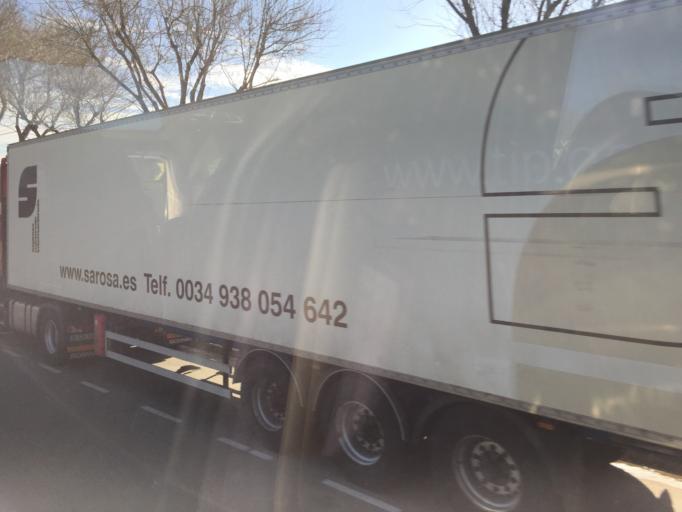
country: ES
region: Catalonia
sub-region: Provincia de Barcelona
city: Sants-Montjuic
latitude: 41.3482
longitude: 2.1333
